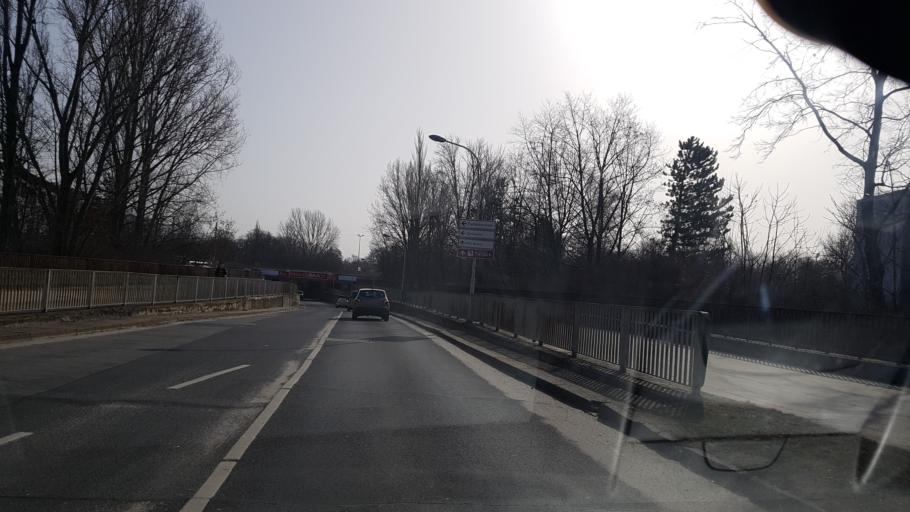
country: DE
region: Brandenburg
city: Cottbus
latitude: 51.7556
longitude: 14.3471
